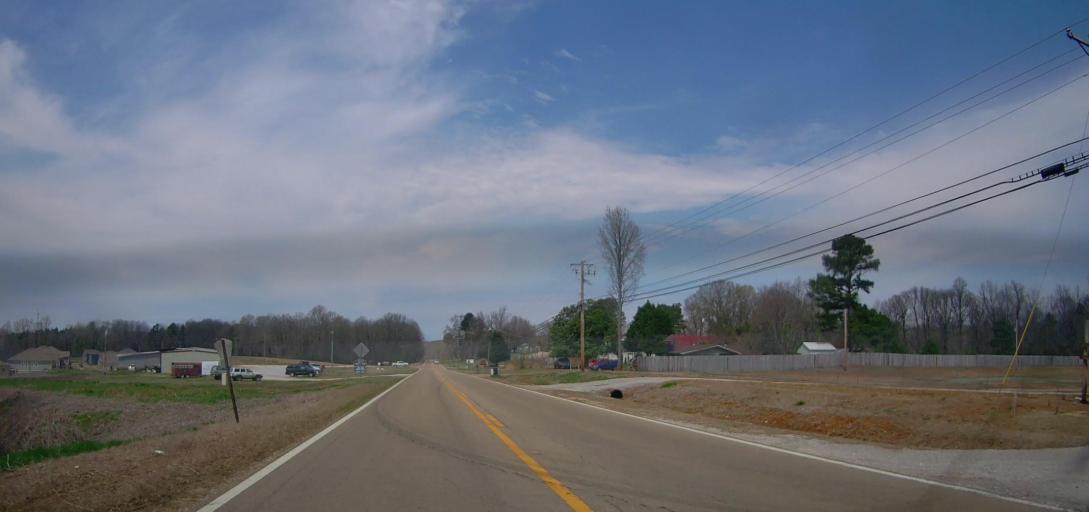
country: US
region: Mississippi
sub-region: Union County
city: New Albany
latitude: 34.4572
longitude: -88.9761
